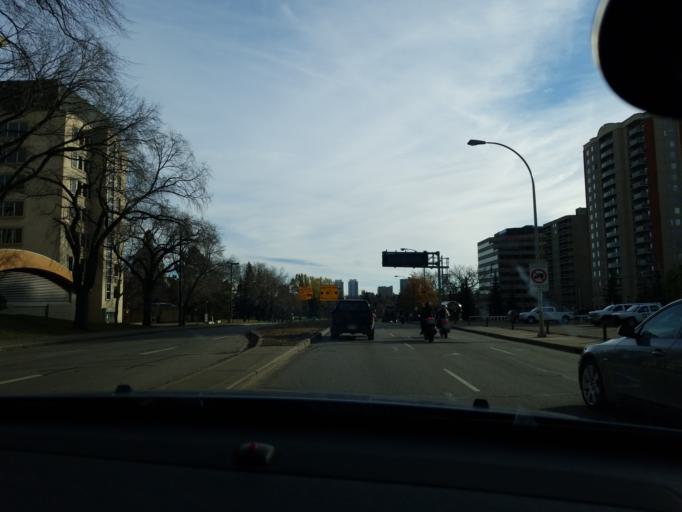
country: CA
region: Alberta
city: Edmonton
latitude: 53.5366
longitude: -113.5085
